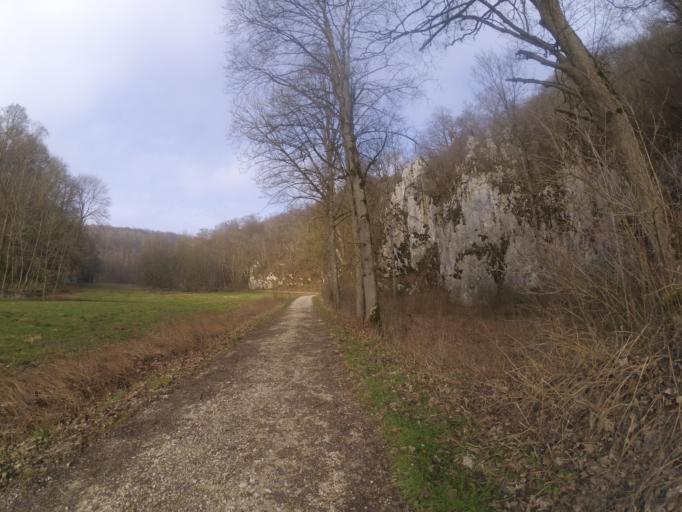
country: DE
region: Baden-Wuerttemberg
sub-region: Tuebingen Region
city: Rechtenstein
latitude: 48.2596
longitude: 9.5481
